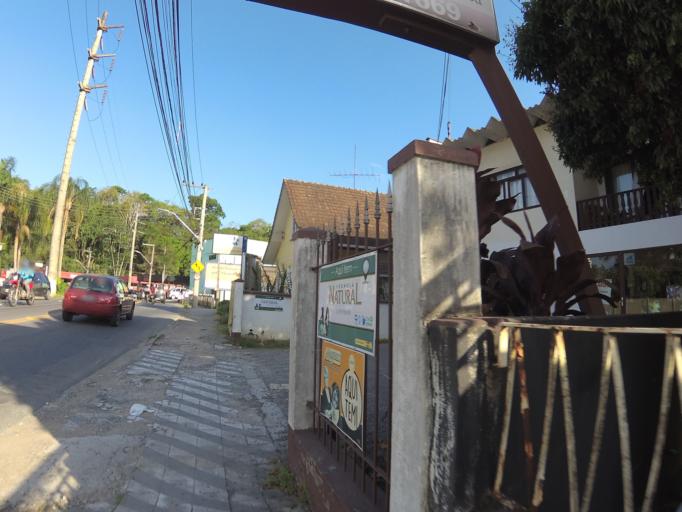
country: BR
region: Santa Catarina
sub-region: Blumenau
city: Blumenau
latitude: -26.9200
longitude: -49.0957
